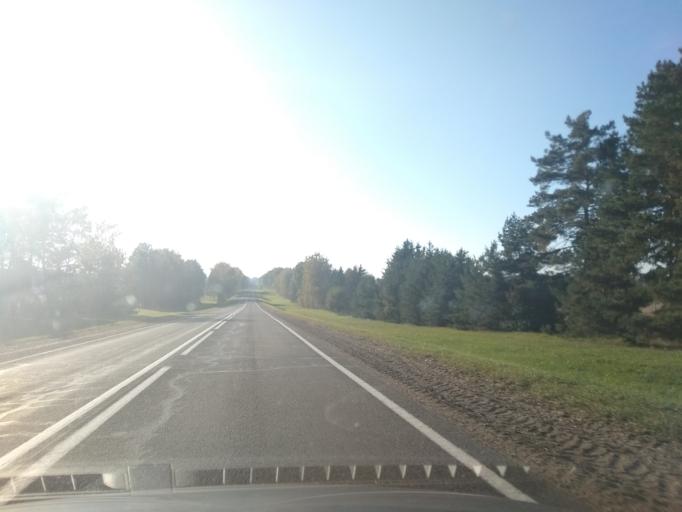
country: BY
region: Grodnenskaya
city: Svislach
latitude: 53.1253
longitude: 24.1195
